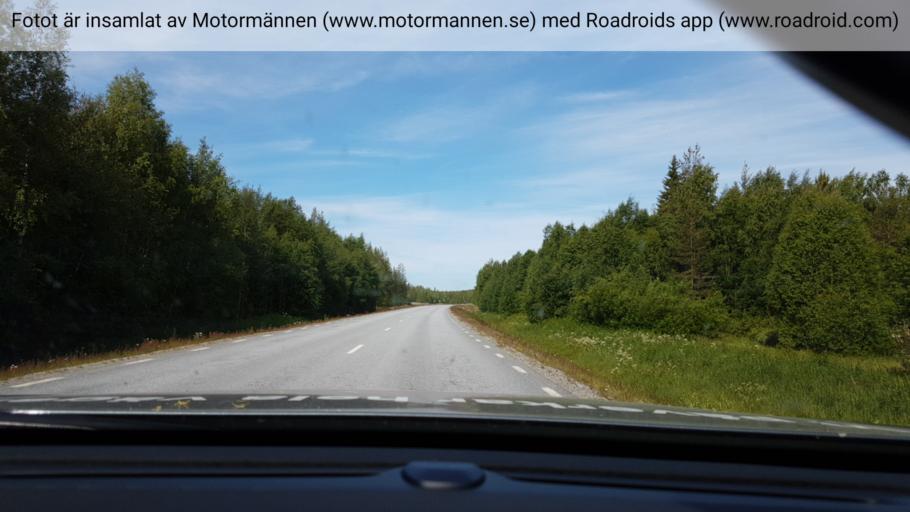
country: SE
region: Vaesterbotten
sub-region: Asele Kommun
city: Asele
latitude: 64.2067
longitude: 16.9919
